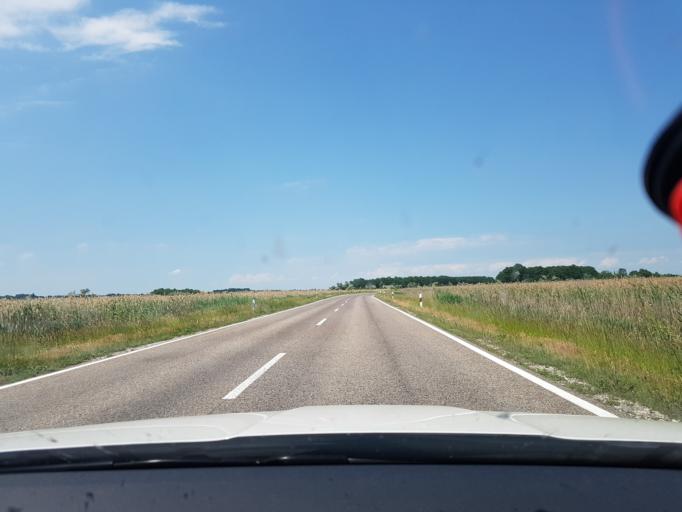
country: HU
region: Hajdu-Bihar
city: Egyek
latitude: 47.5586
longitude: 20.8661
